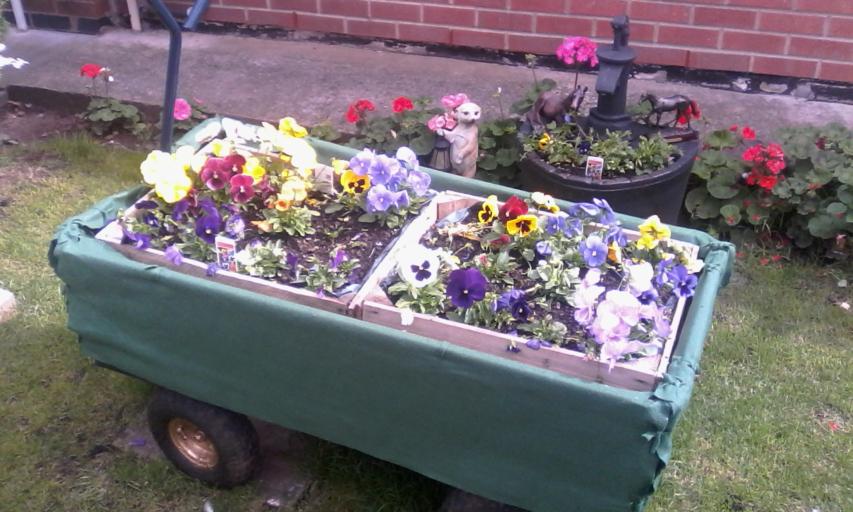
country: GB
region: England
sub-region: Nottinghamshire
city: Arnold
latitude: 52.9753
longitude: -1.0999
